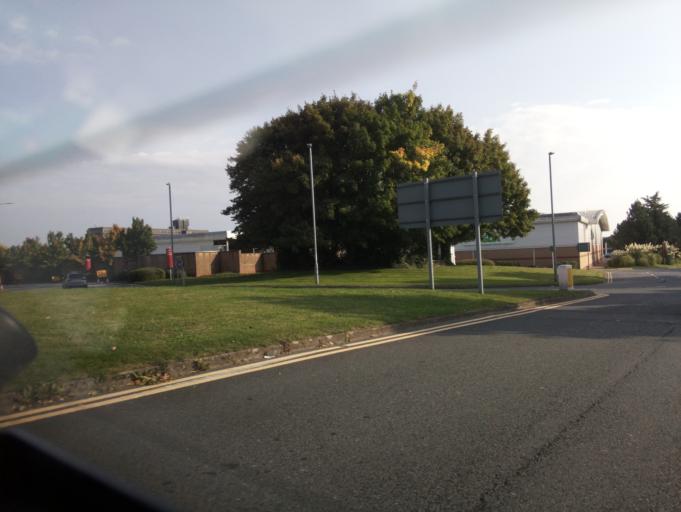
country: GB
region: Wales
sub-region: Torfaen County Borough
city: Cwmbran
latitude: 51.6558
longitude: -3.0246
